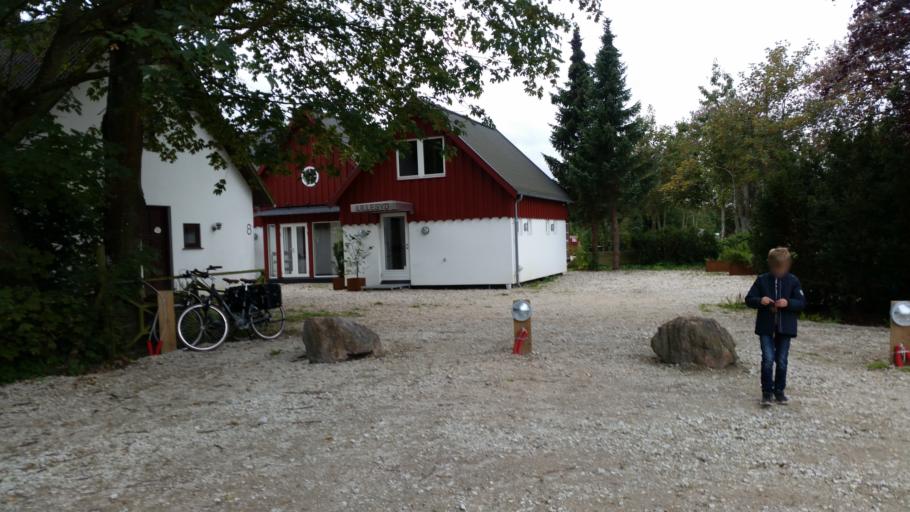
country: DK
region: Zealand
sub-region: Koge Kommune
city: Koge
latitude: 55.4222
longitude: 12.1411
